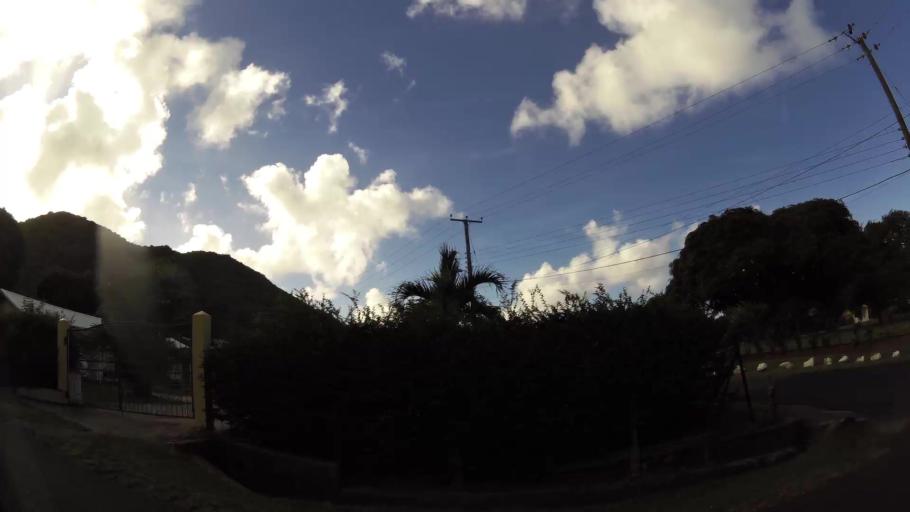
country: LC
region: Gros-Islet
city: Gros Islet
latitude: 14.0697
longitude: -60.9571
